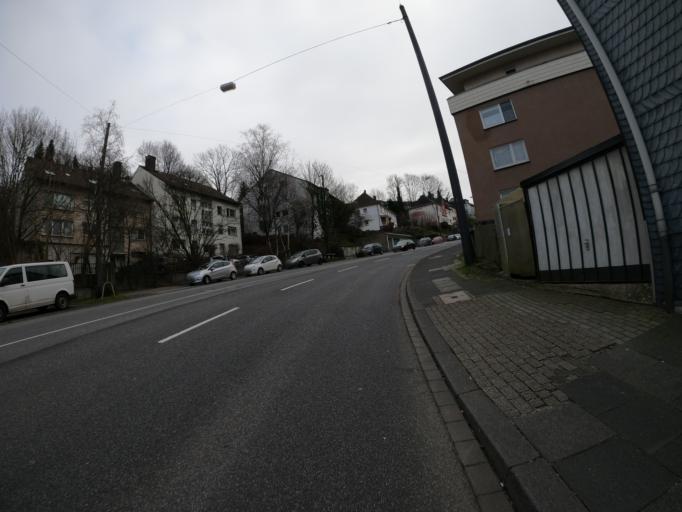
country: DE
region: North Rhine-Westphalia
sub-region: Regierungsbezirk Dusseldorf
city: Wuppertal
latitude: 51.2388
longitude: 7.1468
